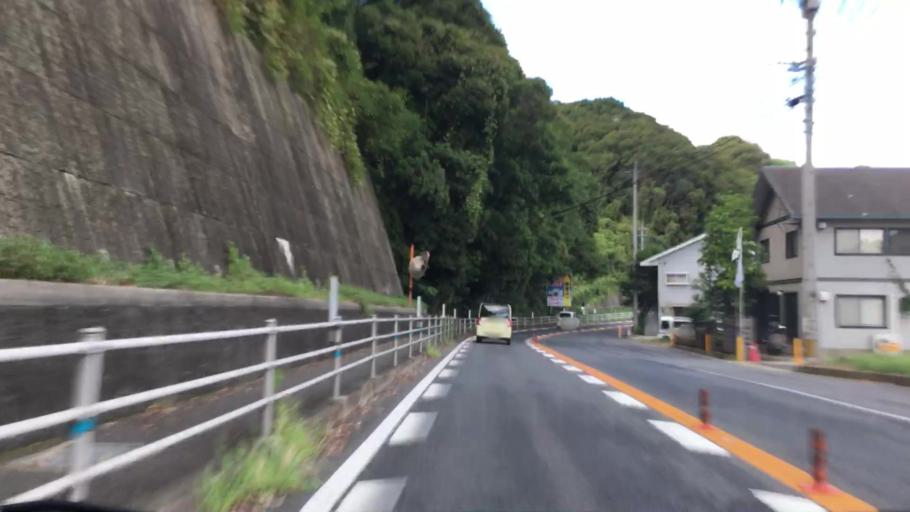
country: JP
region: Nagasaki
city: Sasebo
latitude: 33.1632
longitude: 129.8333
